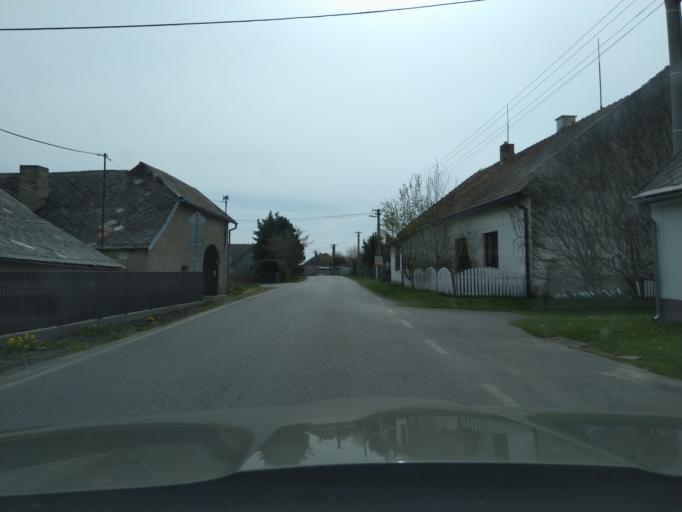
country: CZ
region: Jihocesky
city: Vacov
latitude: 49.1412
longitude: 13.7162
